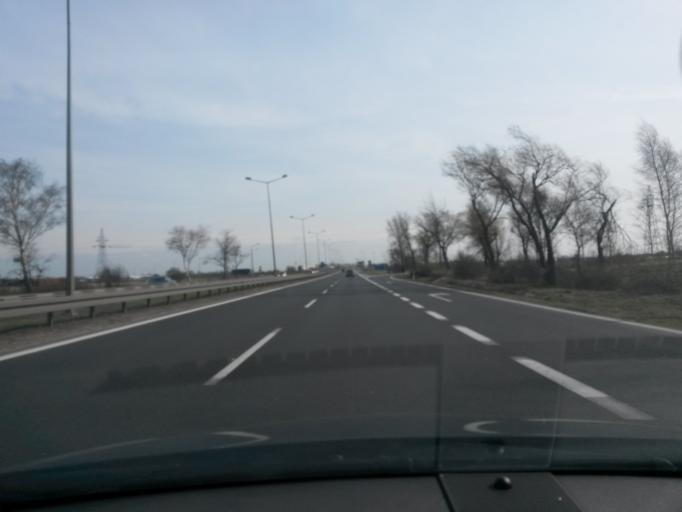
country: PL
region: Greater Poland Voivodeship
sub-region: Powiat poznanski
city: Daszewice
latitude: 52.3505
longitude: 16.9975
